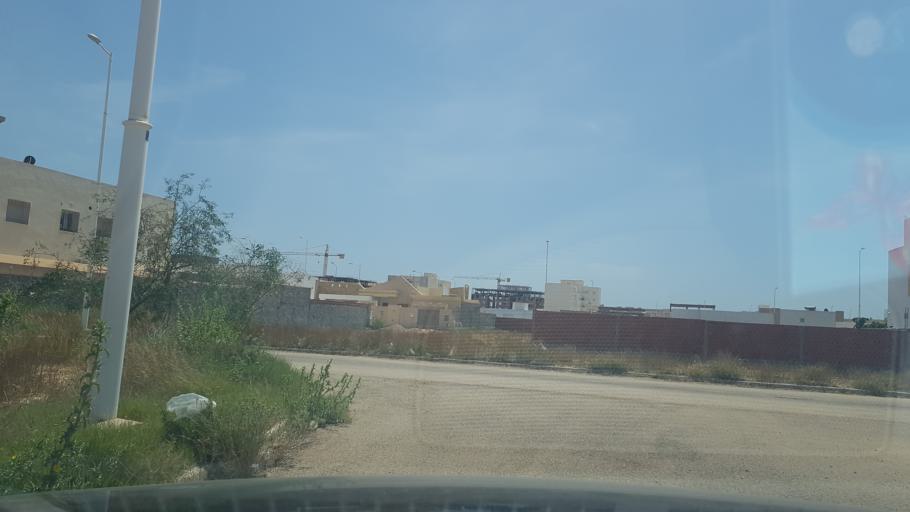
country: TN
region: Safaqis
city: Al Qarmadah
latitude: 34.8357
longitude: 10.7558
